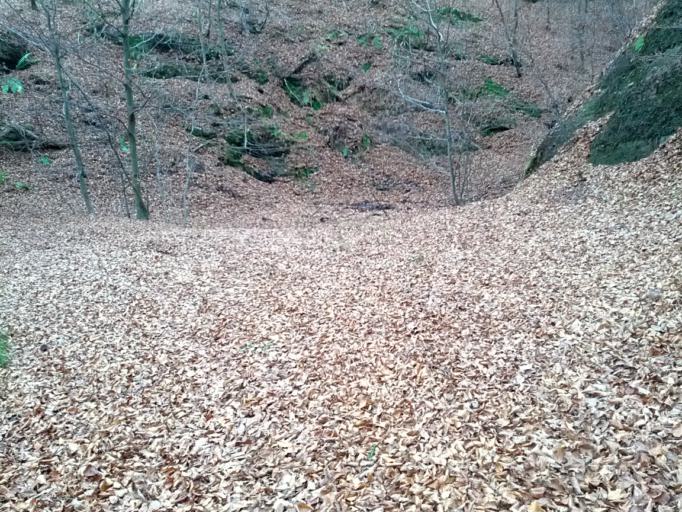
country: DE
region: Thuringia
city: Eisenach
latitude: 50.9420
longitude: 10.3280
